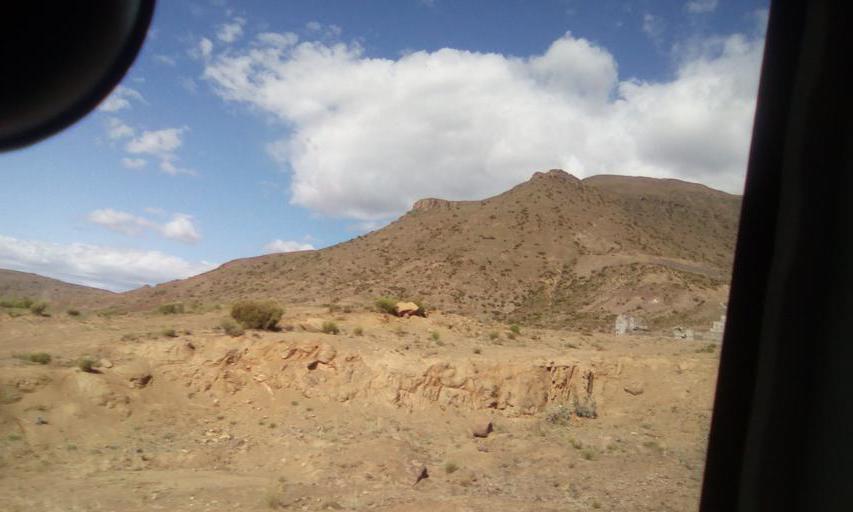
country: LS
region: Qacha's Nek
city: Qacha's Nek
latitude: -30.0106
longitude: 28.1777
